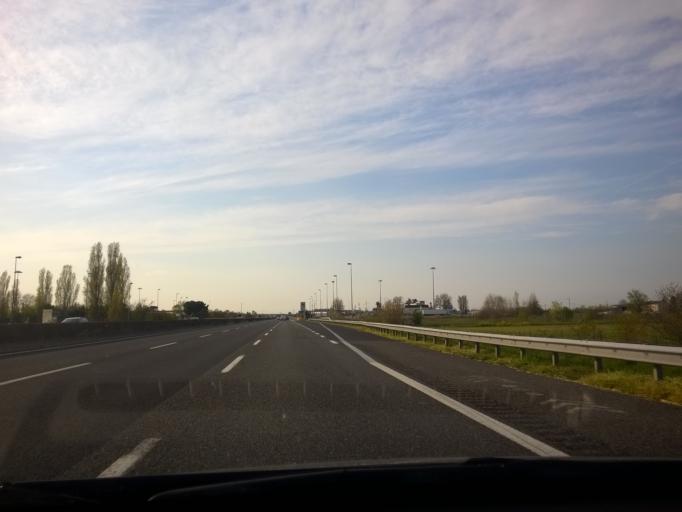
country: IT
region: Emilia-Romagna
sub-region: Forli-Cesena
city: Santa Maria Nuova
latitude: 44.2158
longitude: 12.1796
